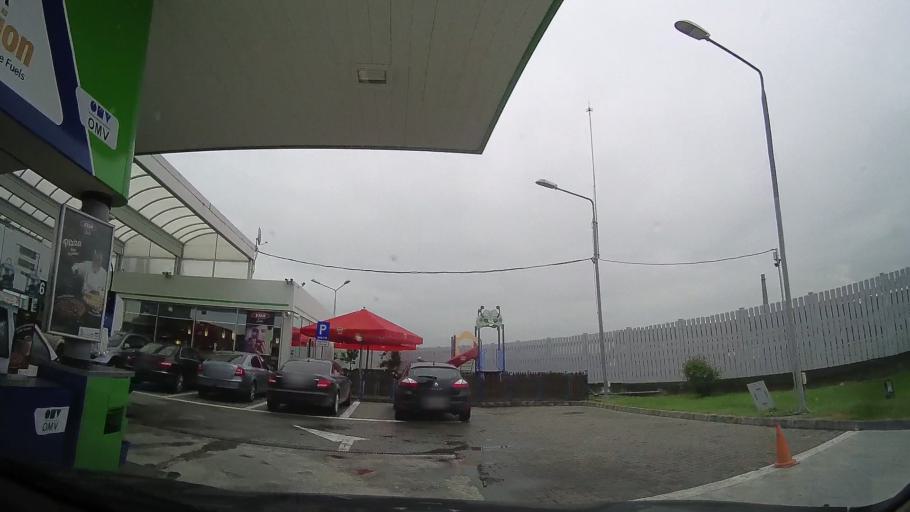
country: RO
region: Mehedinti
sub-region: Comuna Simian
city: Cerneti
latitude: 44.6302
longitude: 22.6854
